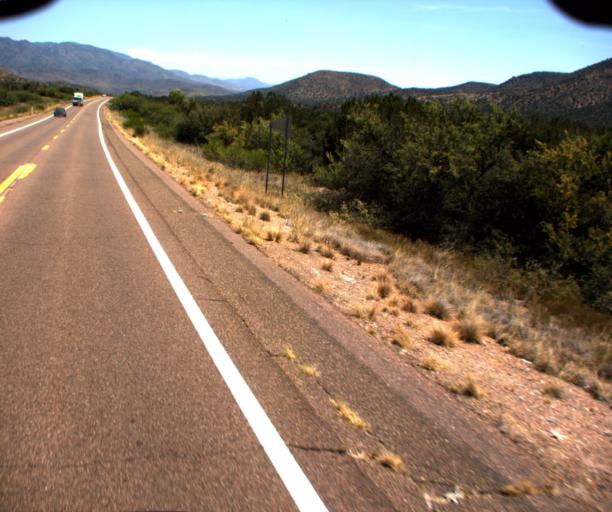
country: US
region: Arizona
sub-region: Gila County
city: Tonto Basin
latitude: 34.0282
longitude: -111.3487
